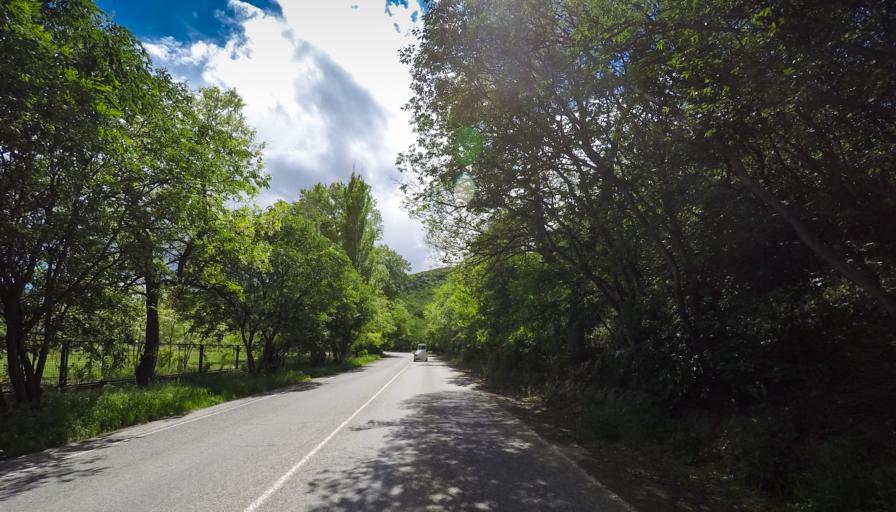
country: GE
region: Mtskheta-Mtianeti
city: Mtskheta
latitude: 41.8352
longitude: 44.7222
